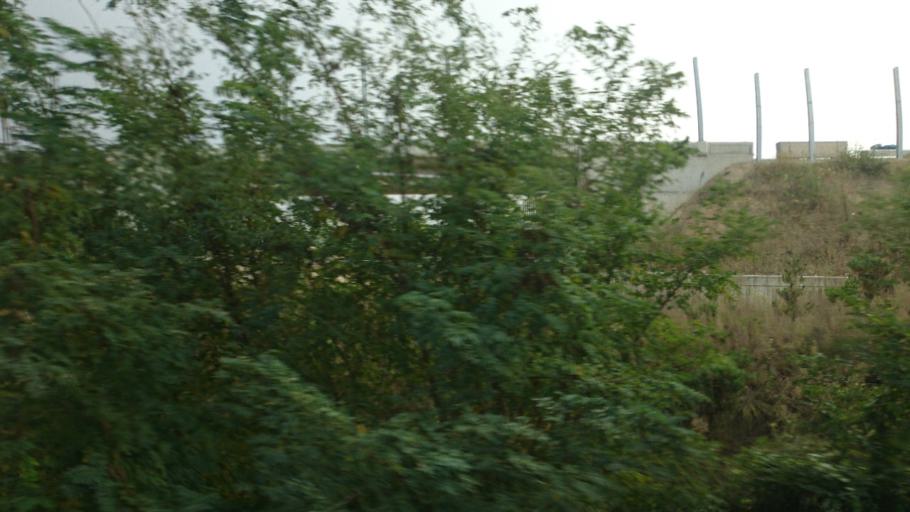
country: KR
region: Gyeongsangbuk-do
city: Hayang
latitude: 35.9001
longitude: 128.8024
